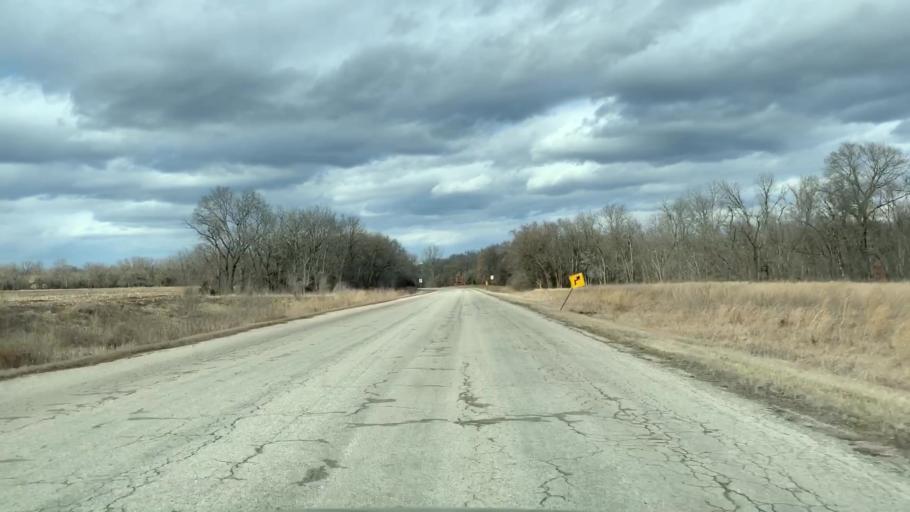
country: US
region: Kansas
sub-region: Neosho County
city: Chanute
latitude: 37.7472
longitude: -95.4704
